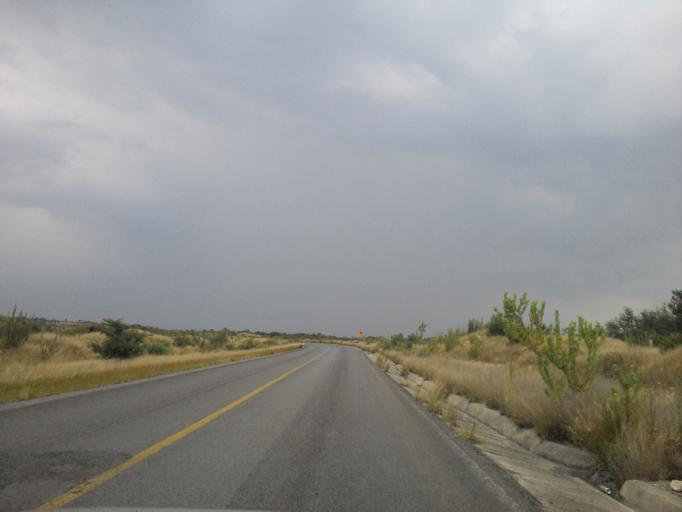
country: MX
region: Jalisco
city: San Diego de Alejandria
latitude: 20.8755
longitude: -102.0767
